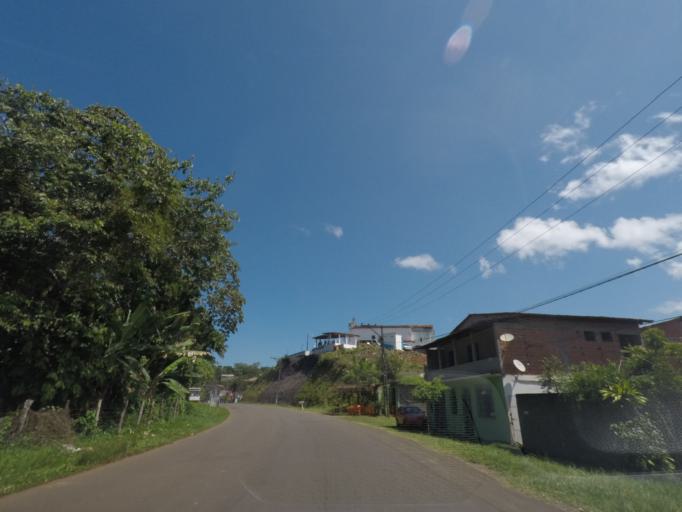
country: BR
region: Bahia
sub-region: Taperoa
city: Taperoa
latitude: -13.5009
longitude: -39.0968
